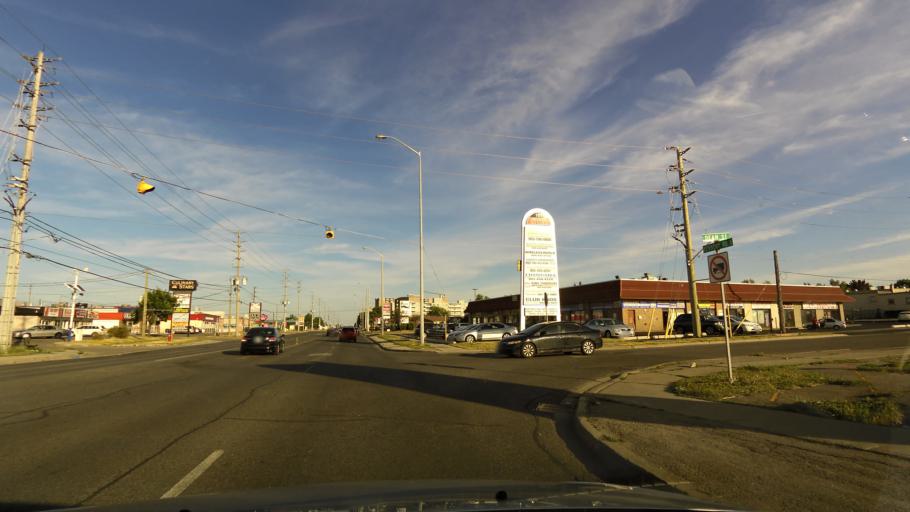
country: CA
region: Ontario
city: Brampton
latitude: 43.6869
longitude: -79.7378
